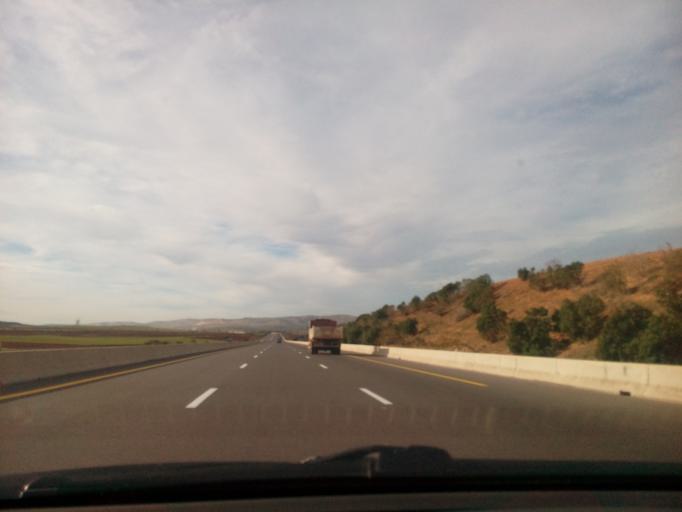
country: DZ
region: Mascara
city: Sig
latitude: 35.5091
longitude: -0.3682
